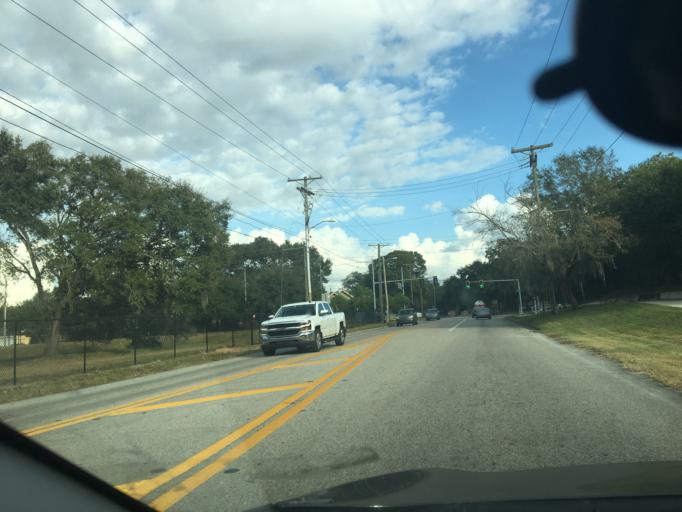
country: US
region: Florida
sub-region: Hillsborough County
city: Temple Terrace
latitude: 28.0435
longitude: -82.4109
